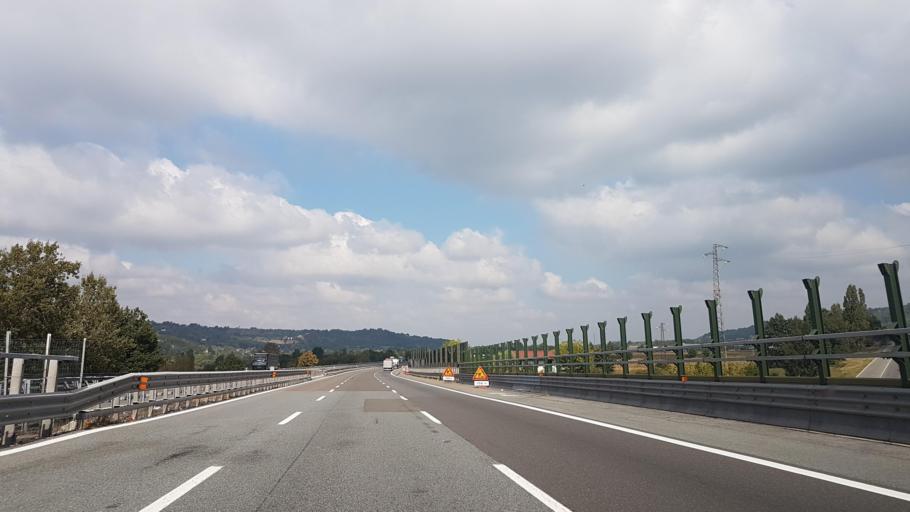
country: IT
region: Piedmont
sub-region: Provincia di Alessandria
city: Rocca Grimalda
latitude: 44.6591
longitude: 8.6593
